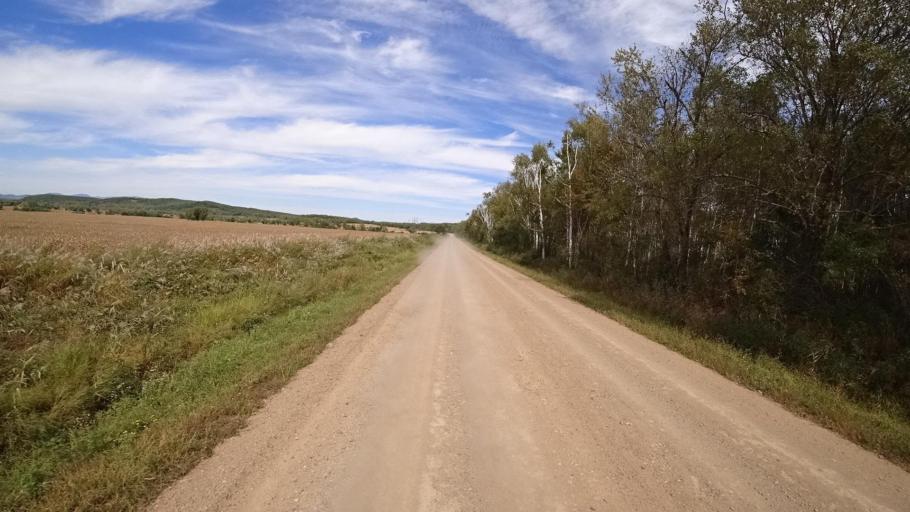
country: RU
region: Primorskiy
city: Yakovlevka
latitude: 44.5840
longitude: 133.6008
